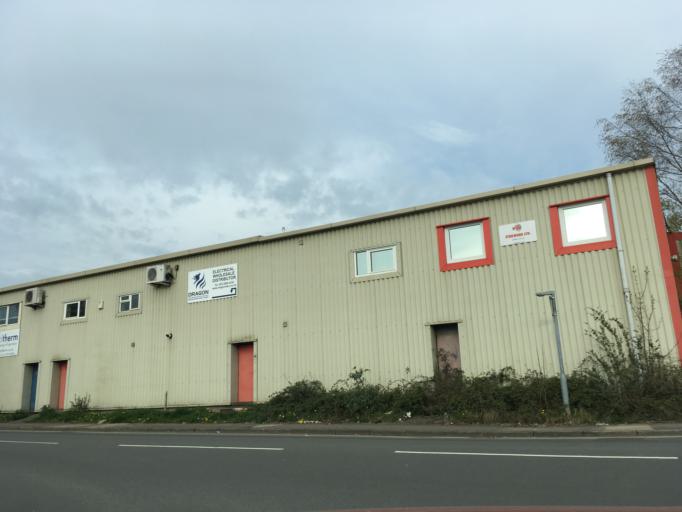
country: GB
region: Wales
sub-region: Caerphilly County Borough
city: Bedwas
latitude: 51.5932
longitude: -3.2105
